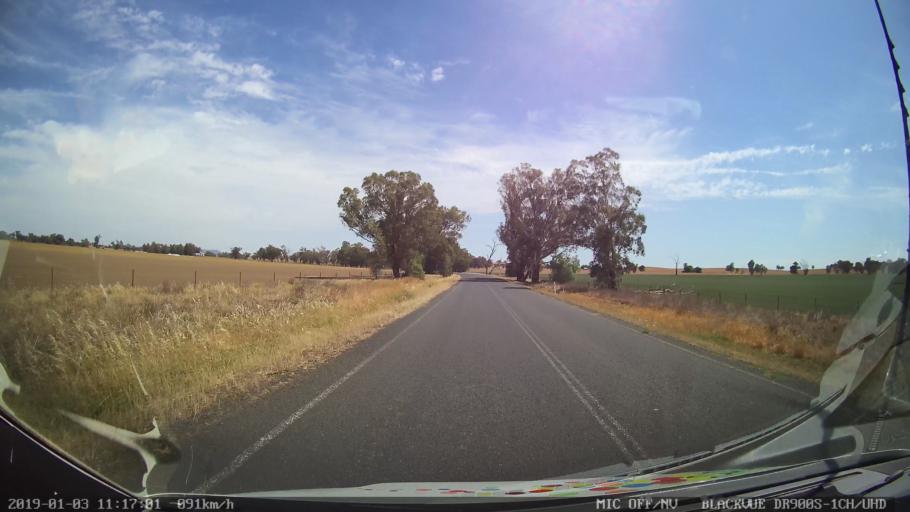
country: AU
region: New South Wales
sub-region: Young
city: Young
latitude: -34.1442
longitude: 148.2677
